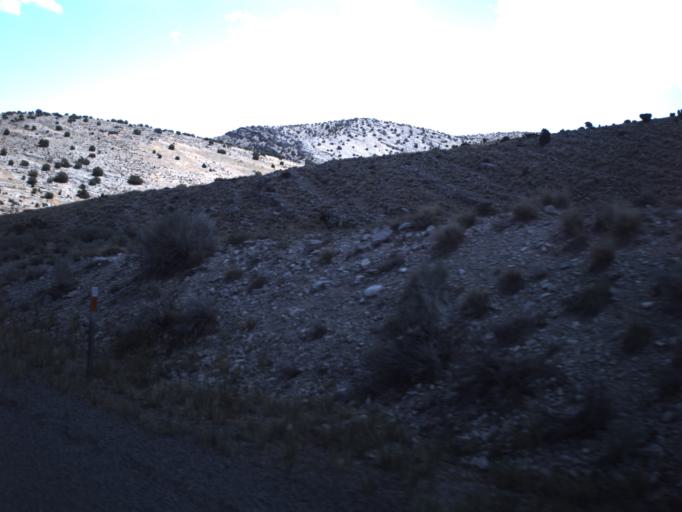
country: US
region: Utah
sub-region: Beaver County
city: Milford
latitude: 39.0796
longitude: -113.6074
